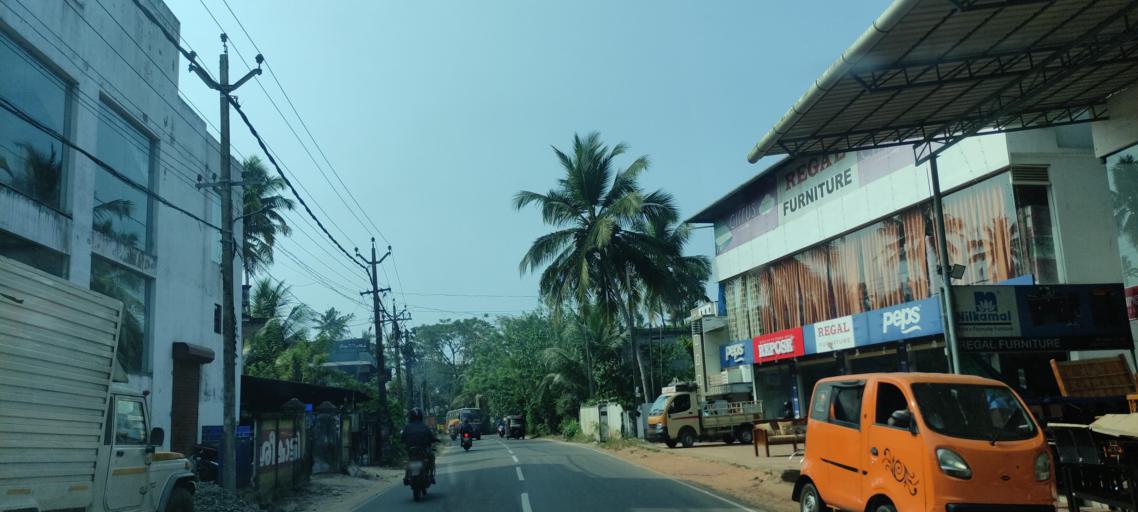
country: IN
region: Kerala
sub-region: Alappuzha
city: Vayalar
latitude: 9.6948
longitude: 76.3284
